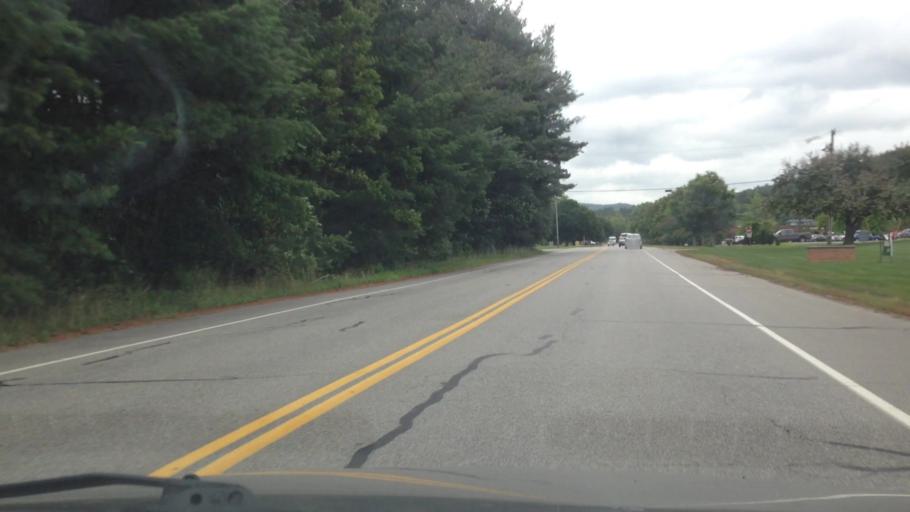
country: US
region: New Hampshire
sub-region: Cheshire County
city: Keene
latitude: 42.9177
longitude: -72.2627
